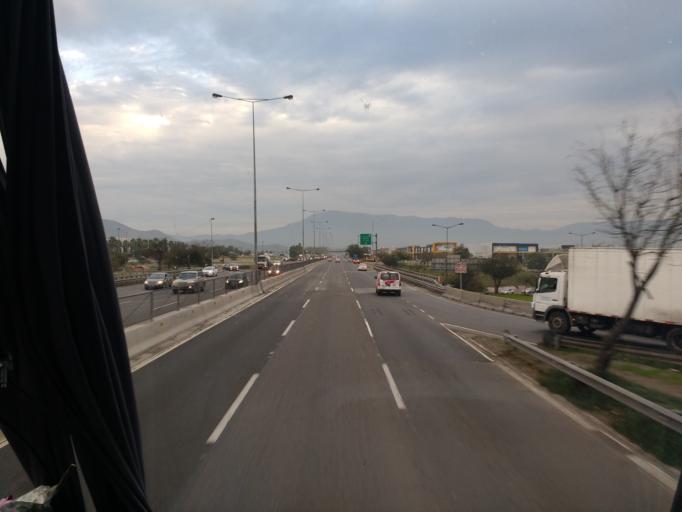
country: CL
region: Santiago Metropolitan
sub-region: Provincia de Santiago
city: Lo Prado
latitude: -33.4461
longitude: -70.7774
